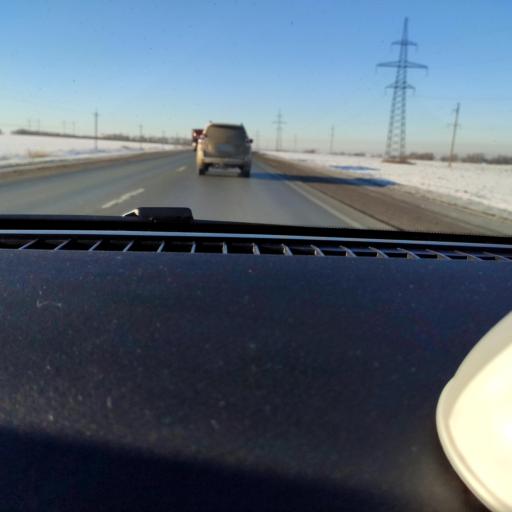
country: RU
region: Samara
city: Smyshlyayevka
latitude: 53.1477
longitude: 50.4907
